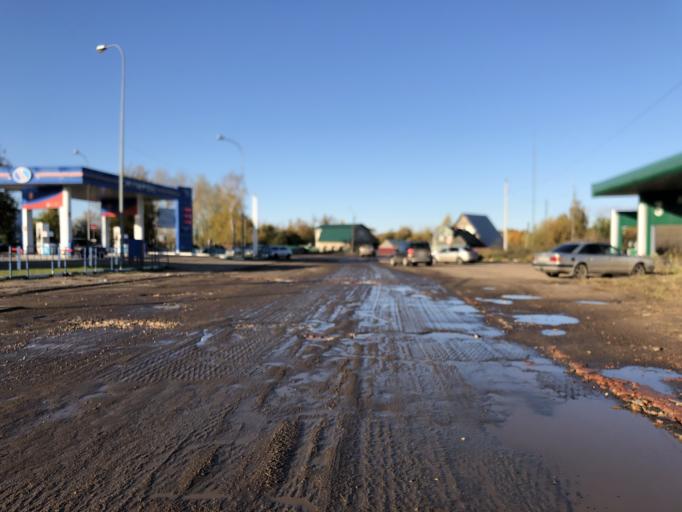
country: RU
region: Tverskaya
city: Rzhev
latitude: 56.2401
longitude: 34.3467
